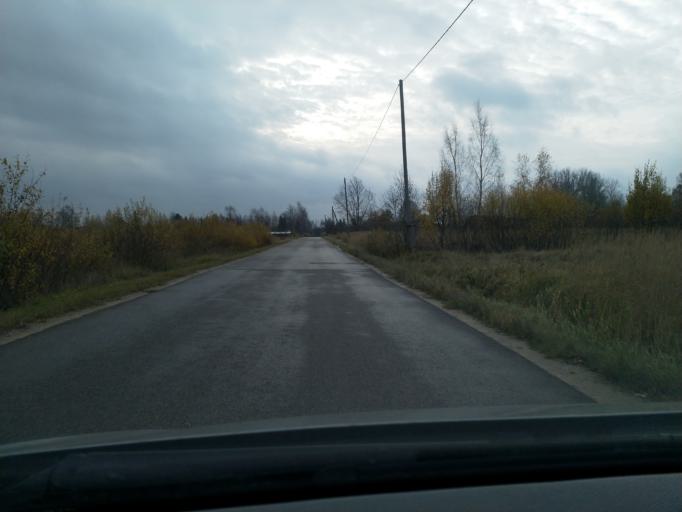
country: LV
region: Kuldigas Rajons
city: Kuldiga
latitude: 56.9797
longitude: 21.9765
